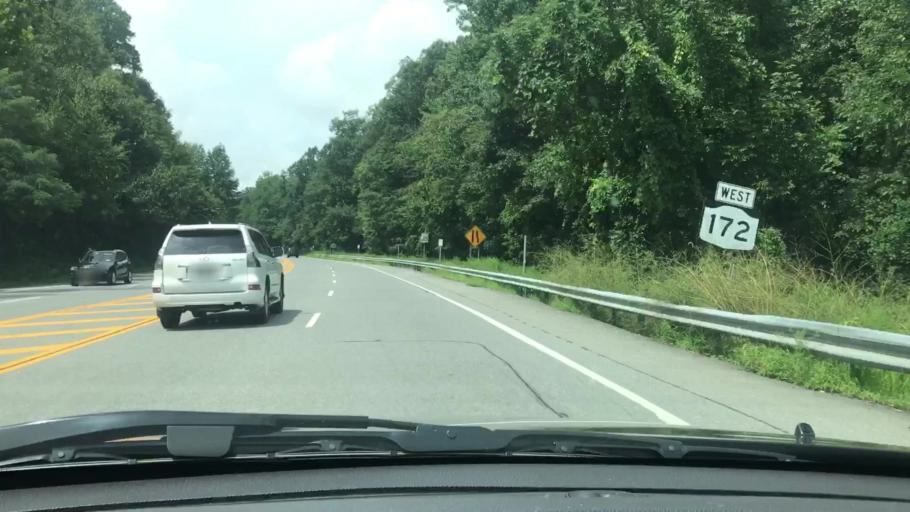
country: US
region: New York
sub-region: Westchester County
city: Mount Kisco
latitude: 41.1957
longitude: -73.6874
